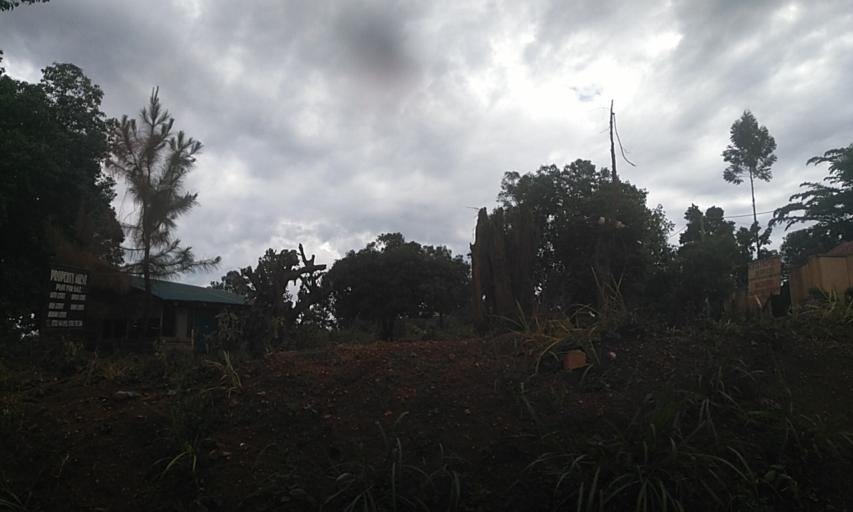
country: UG
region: Central Region
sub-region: Wakiso District
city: Kireka
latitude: 0.4029
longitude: 32.6323
